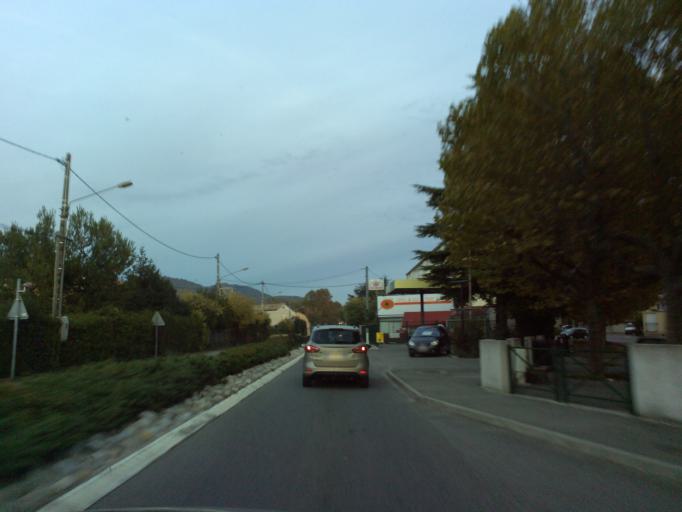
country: FR
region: Provence-Alpes-Cote d'Azur
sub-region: Departement des Alpes-de-Haute-Provence
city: Malijai
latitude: 44.0464
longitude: 6.0306
